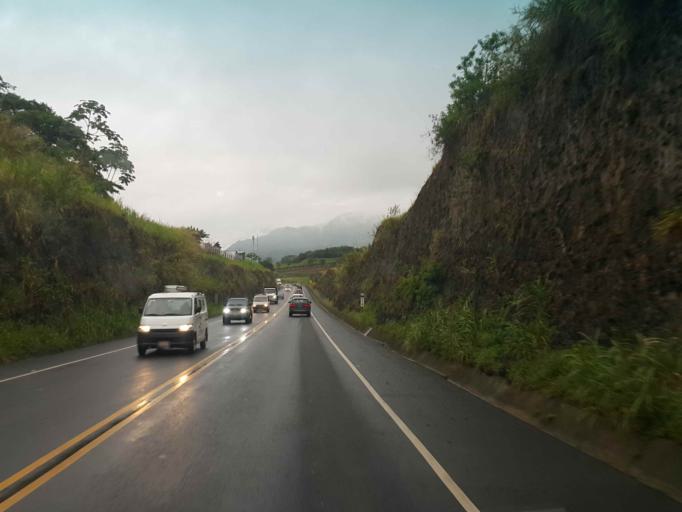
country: CR
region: Heredia
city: Colon
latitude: 9.9461
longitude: -84.2312
